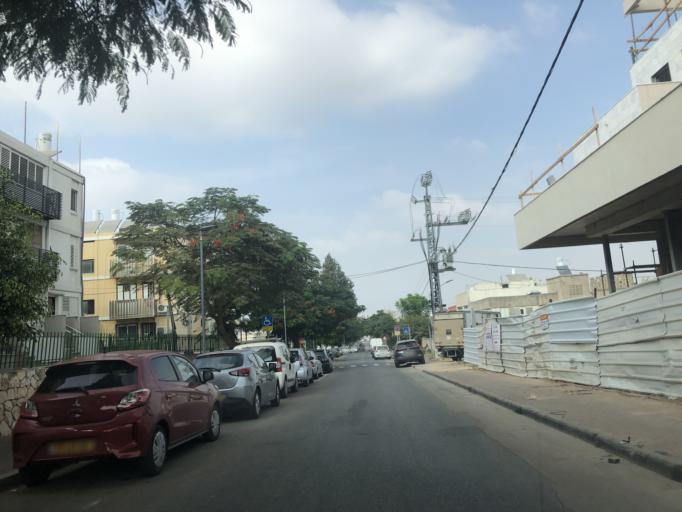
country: IL
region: Central District
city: Rosh Ha'Ayin
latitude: 32.0951
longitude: 34.9525
